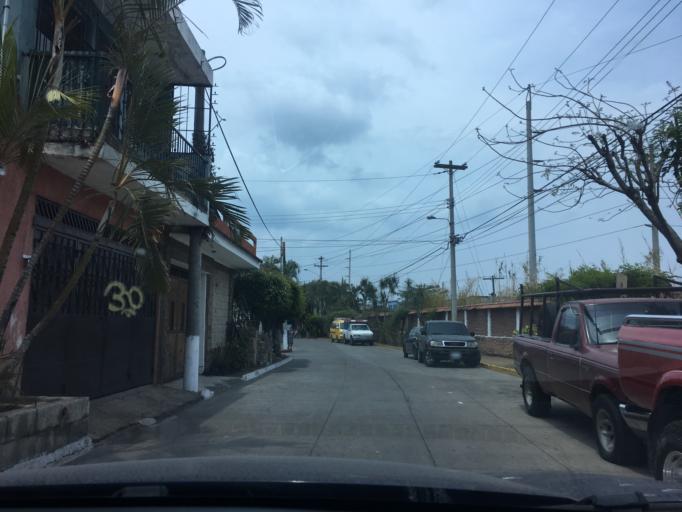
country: GT
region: Guatemala
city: Petapa
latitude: 14.5082
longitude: -90.5588
